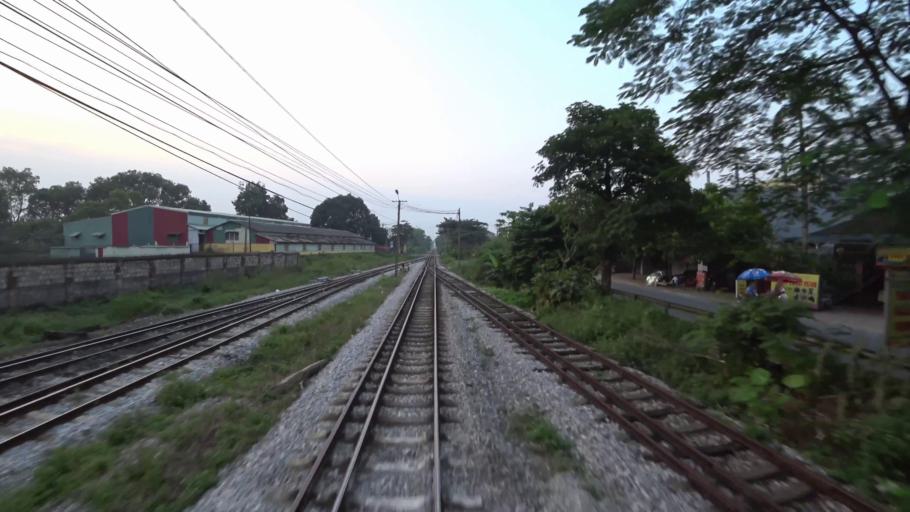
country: VN
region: Ha Noi
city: Dong Anh
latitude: 21.1406
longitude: 105.8658
